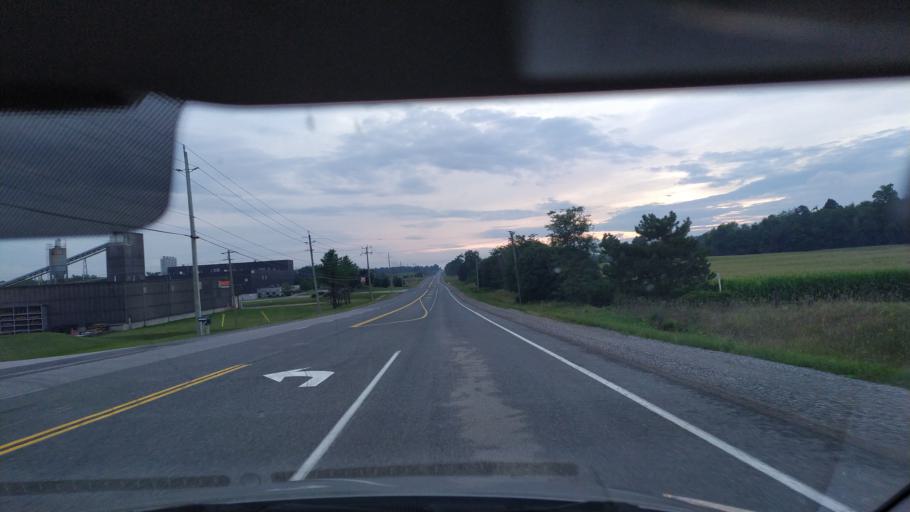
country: CA
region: Ontario
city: Kitchener
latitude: 43.3296
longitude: -80.4580
